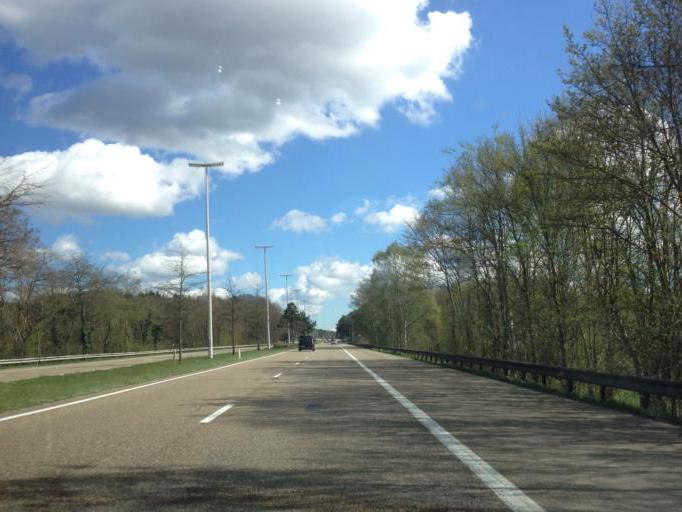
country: BE
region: Flanders
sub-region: Provincie Limburg
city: Genk
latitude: 50.9738
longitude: 5.5412
